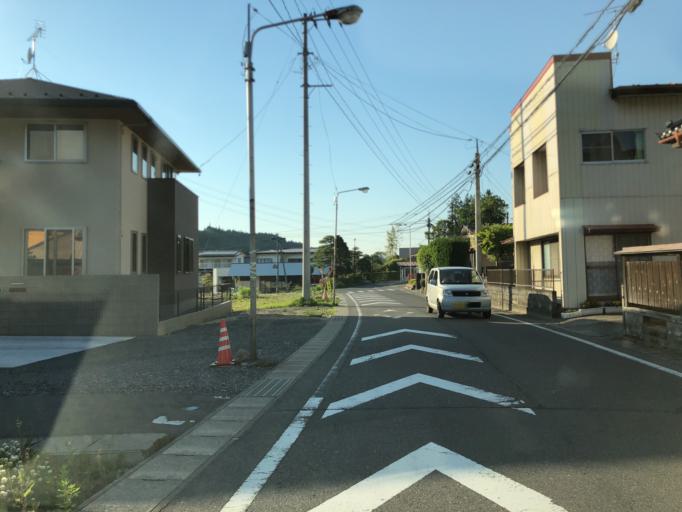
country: JP
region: Ibaraki
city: Daigo
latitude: 36.9398
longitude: 140.4441
